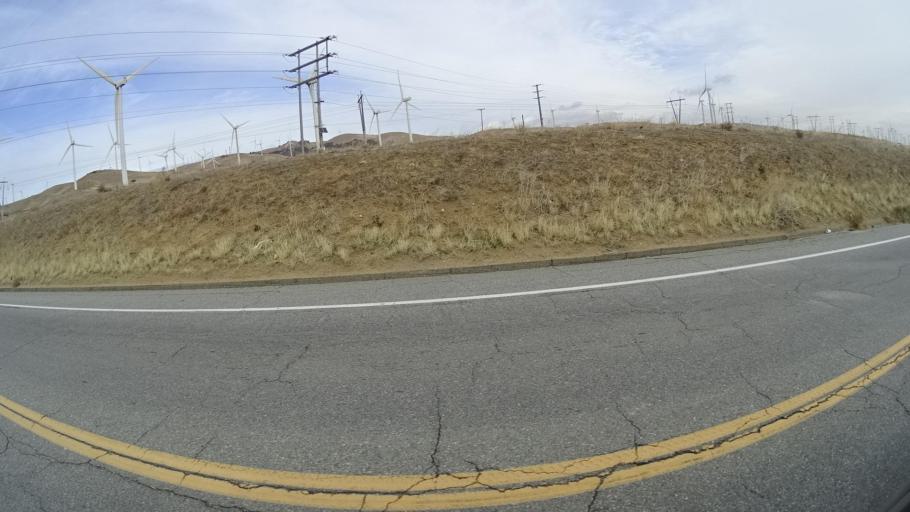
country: US
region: California
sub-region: Kern County
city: Tehachapi
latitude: 35.0520
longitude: -118.3576
